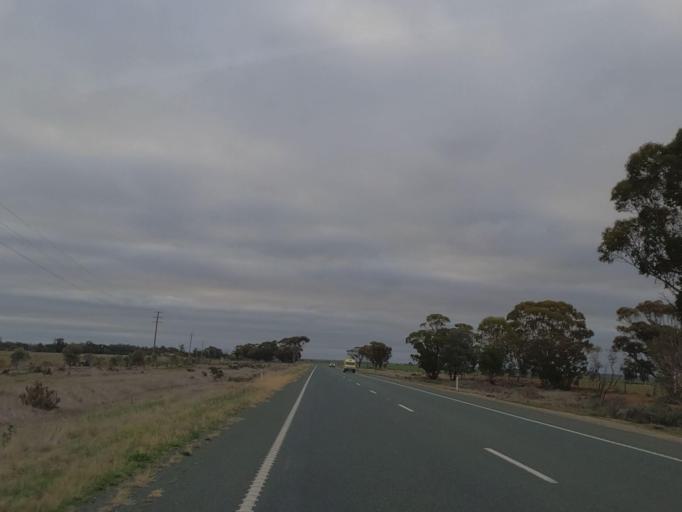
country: AU
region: Victoria
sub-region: Swan Hill
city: Swan Hill
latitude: -35.5659
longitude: 143.7839
